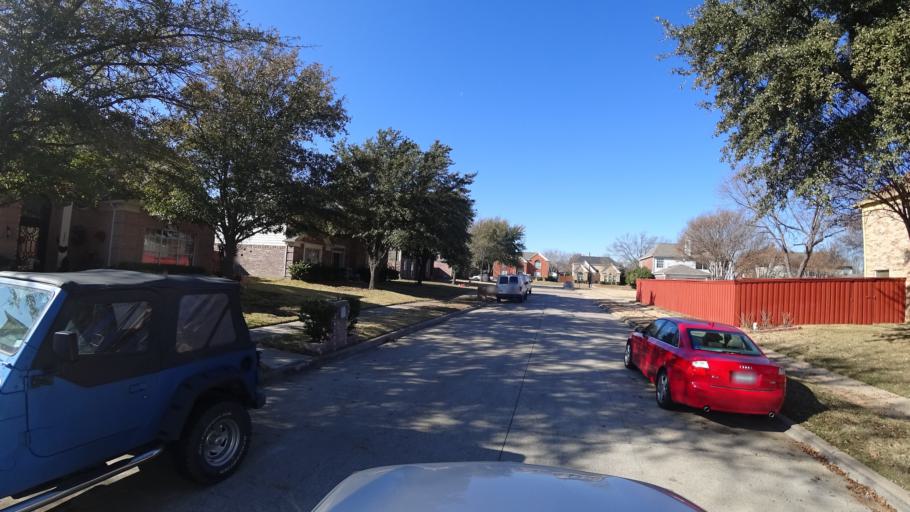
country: US
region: Texas
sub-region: Denton County
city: Lewisville
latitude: 33.0182
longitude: -97.0331
